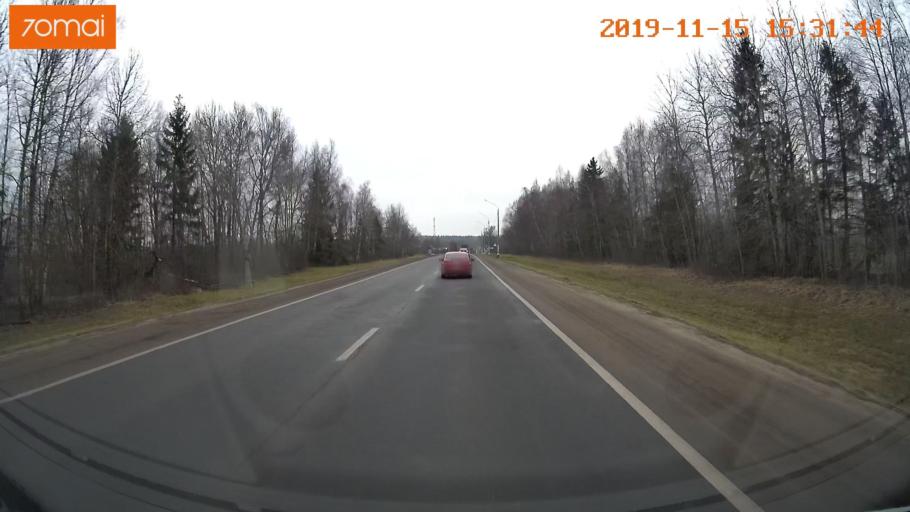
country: RU
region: Jaroslavl
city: Danilov
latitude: 58.0969
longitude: 40.1052
